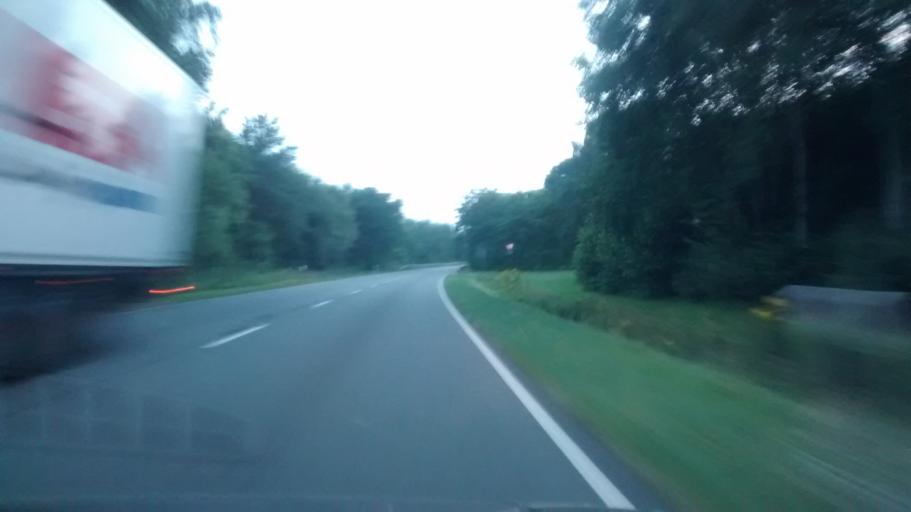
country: DE
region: Lower Saxony
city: Haselunne
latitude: 52.6857
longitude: 7.4653
